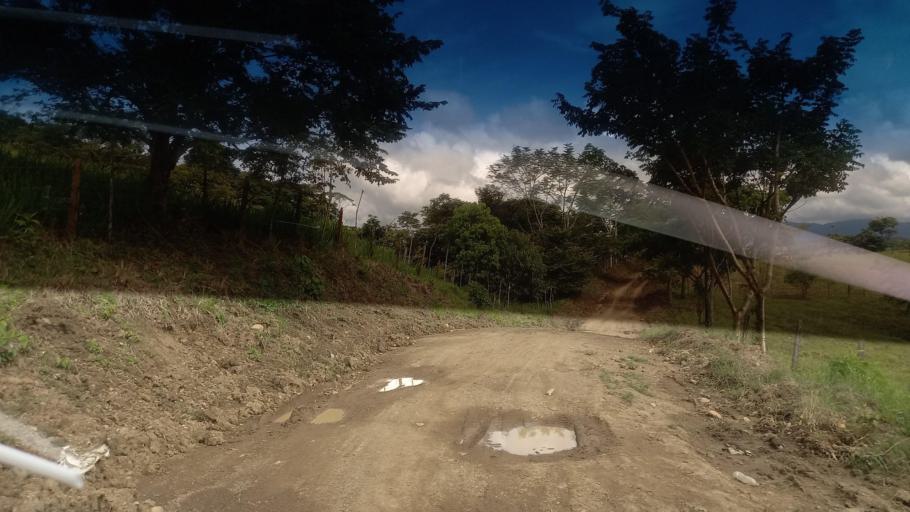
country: NI
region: Jinotega
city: San Jose de Bocay
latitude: 13.4077
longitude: -85.7025
